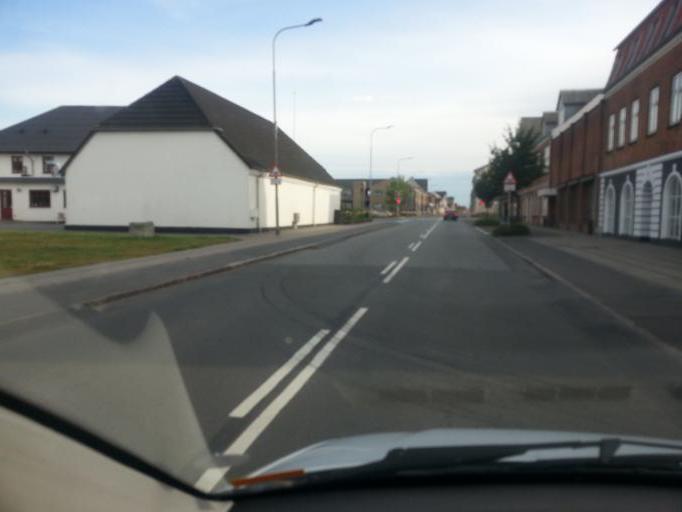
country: DK
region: South Denmark
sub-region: Vejen Kommune
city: Holsted
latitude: 55.4856
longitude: 8.9128
